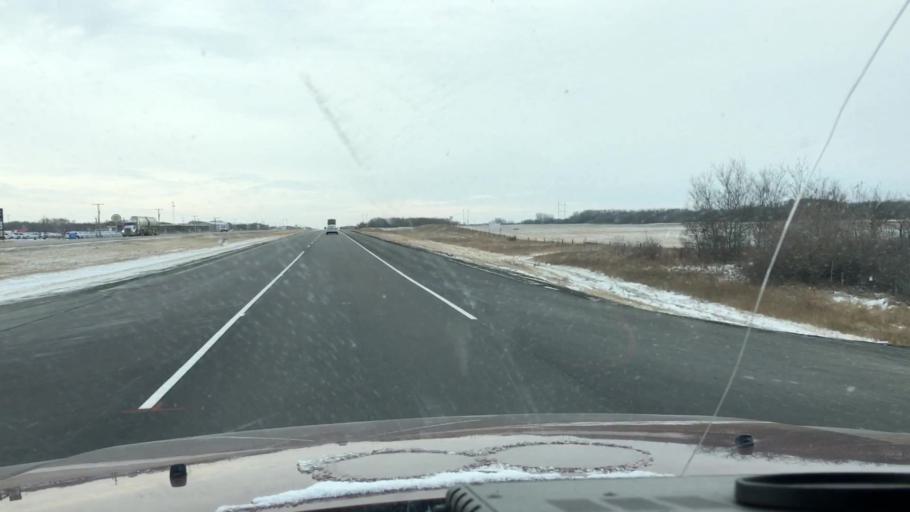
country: CA
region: Saskatchewan
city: Saskatoon
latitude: 51.9690
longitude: -106.5536
